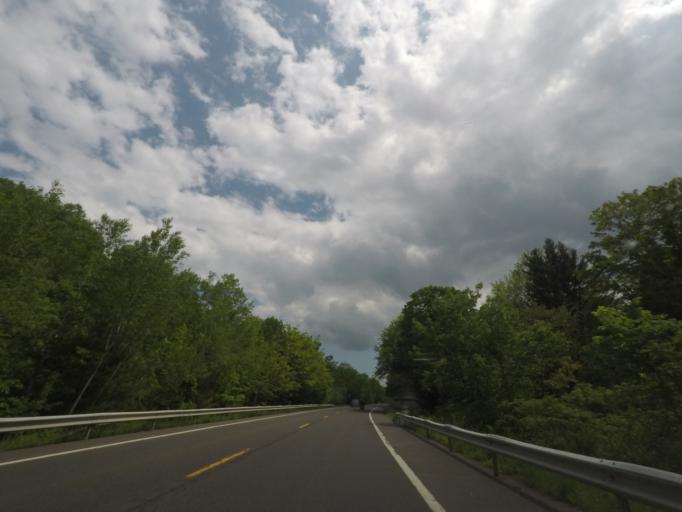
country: US
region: New York
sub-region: Dutchess County
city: Pine Plains
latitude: 42.1040
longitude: -73.6918
